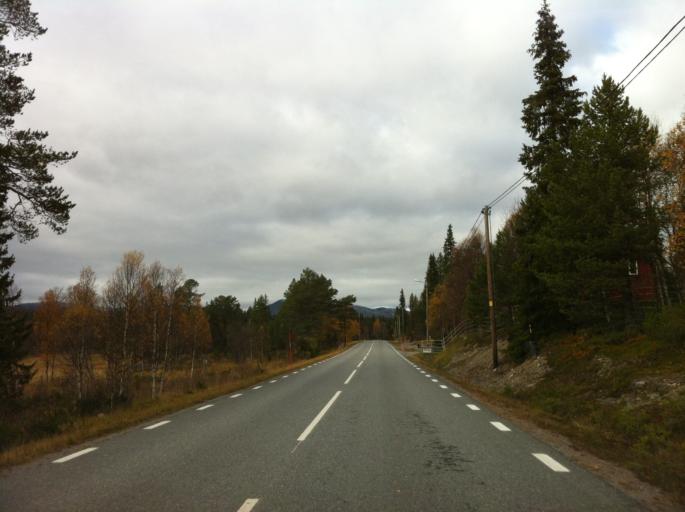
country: NO
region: Hedmark
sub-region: Engerdal
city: Engerdal
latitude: 62.0670
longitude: 12.3169
